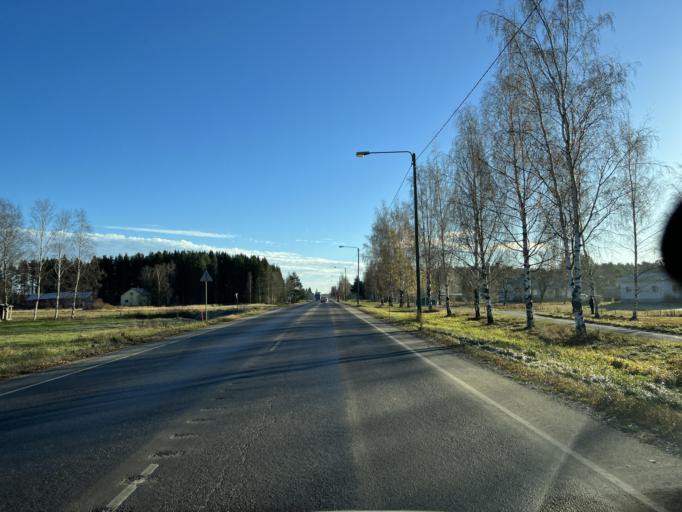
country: FI
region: Northern Ostrobothnia
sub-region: Nivala-Haapajaervi
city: Nivala
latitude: 63.9475
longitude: 24.9265
